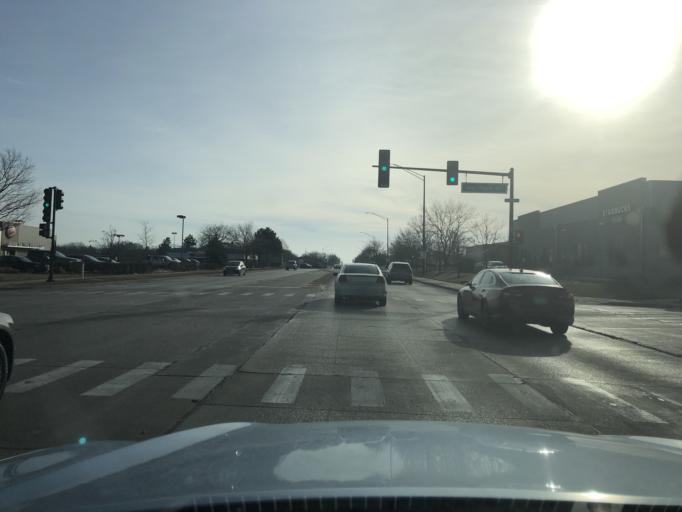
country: US
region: Illinois
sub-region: DuPage County
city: Roselle
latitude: 42.0086
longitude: -88.0802
